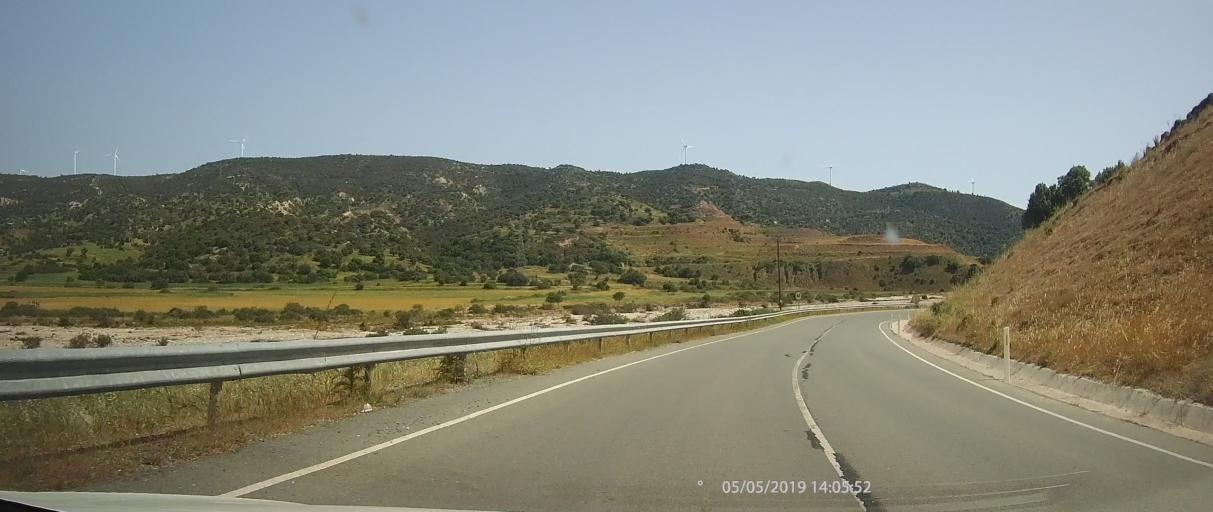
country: CY
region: Limassol
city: Pissouri
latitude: 34.7485
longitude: 32.6092
